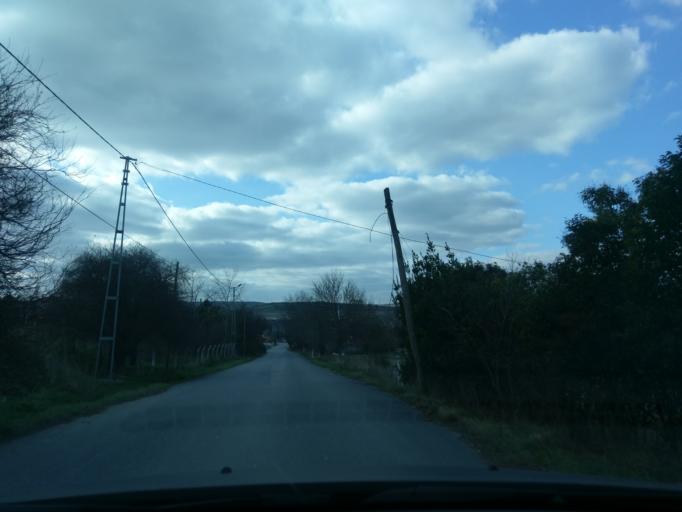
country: TR
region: Istanbul
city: Durusu
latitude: 41.3060
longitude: 28.6841
